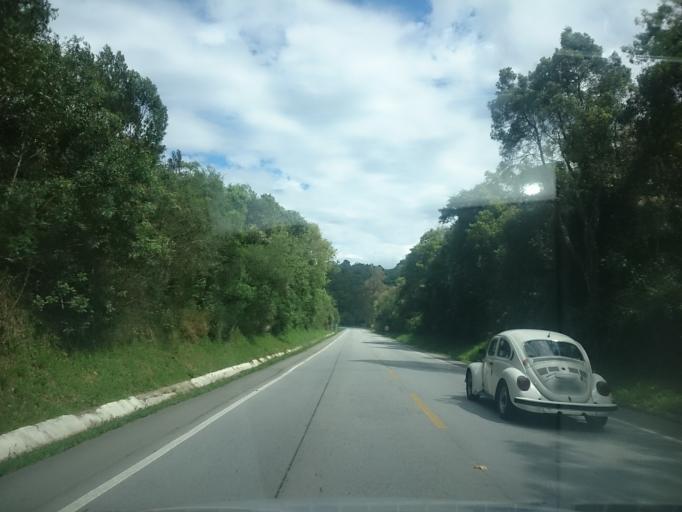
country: BR
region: Santa Catarina
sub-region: Anitapolis
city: Anitapolis
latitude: -27.6971
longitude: -49.2352
